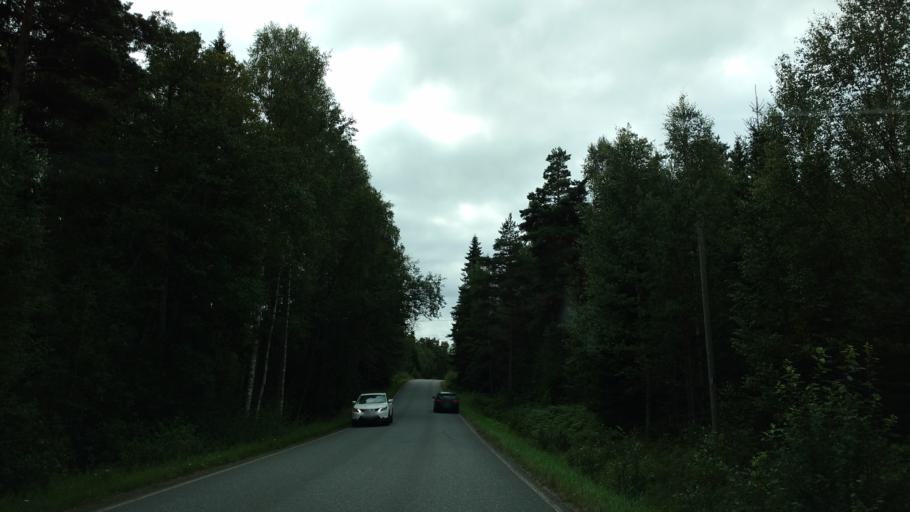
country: FI
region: Varsinais-Suomi
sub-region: Aboland-Turunmaa
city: Dragsfjaerd
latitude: 59.9516
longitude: 22.4194
